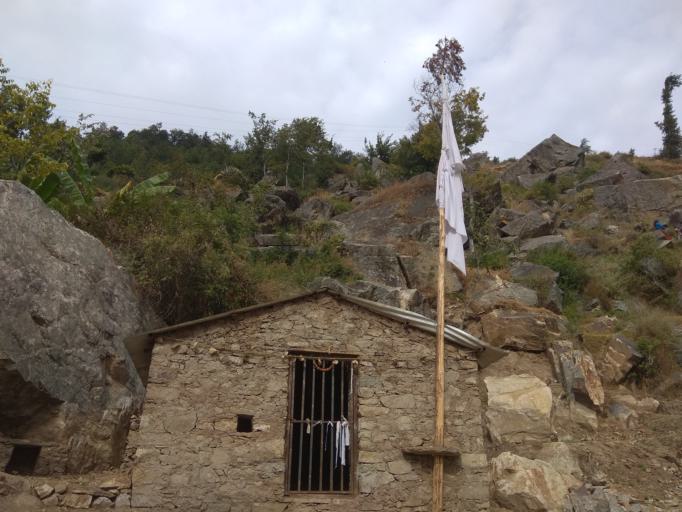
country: NP
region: Mid Western
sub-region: Bheri Zone
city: Dailekh
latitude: 29.2457
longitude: 81.6590
